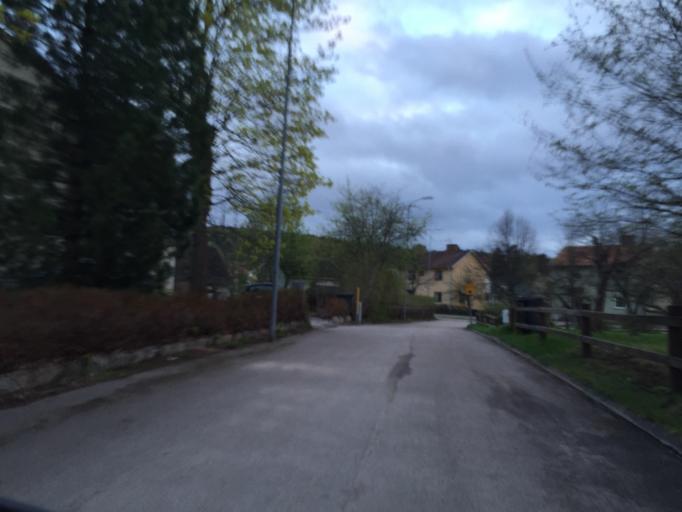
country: SE
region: Dalarna
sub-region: Ludvika Kommun
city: Ludvika
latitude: 60.1456
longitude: 15.1941
